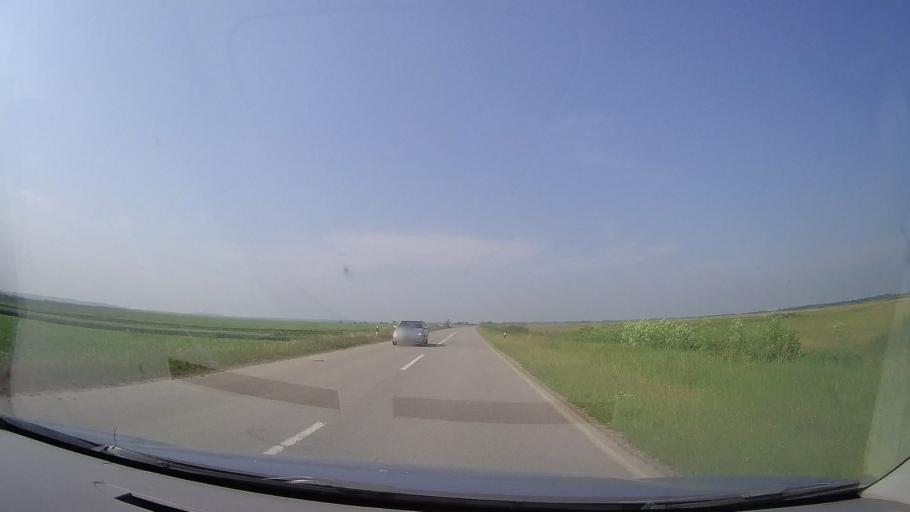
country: RS
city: Jasa Tomic
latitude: 45.4128
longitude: 20.8294
